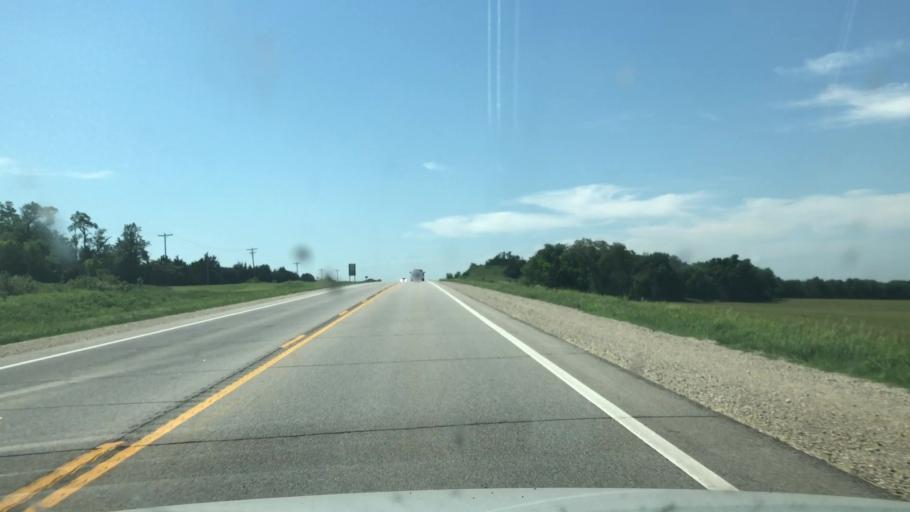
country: US
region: Kansas
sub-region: Cowley County
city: Winfield
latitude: 37.3738
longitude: -97.0071
